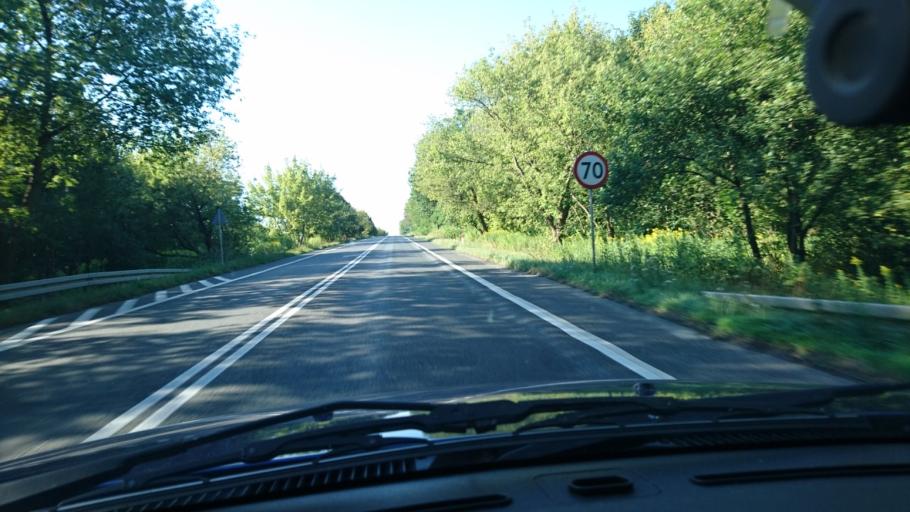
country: PL
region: Silesian Voivodeship
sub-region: Powiat gliwicki
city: Pyskowice
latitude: 50.3547
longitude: 18.6447
